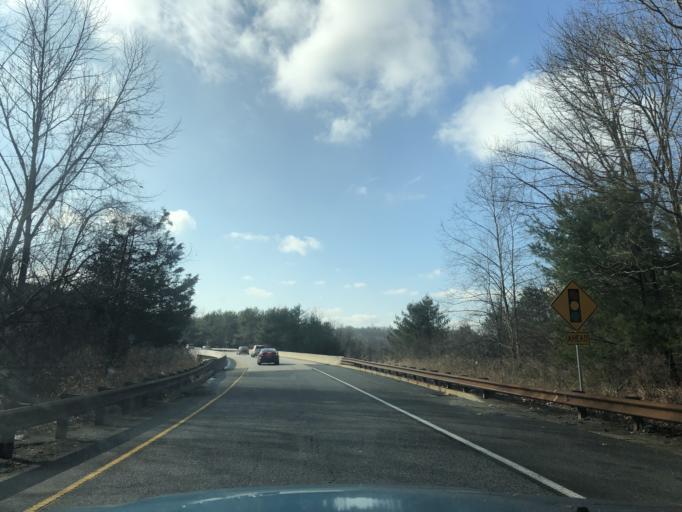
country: US
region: Pennsylvania
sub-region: Delaware County
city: Media
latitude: 39.9390
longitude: -75.3636
